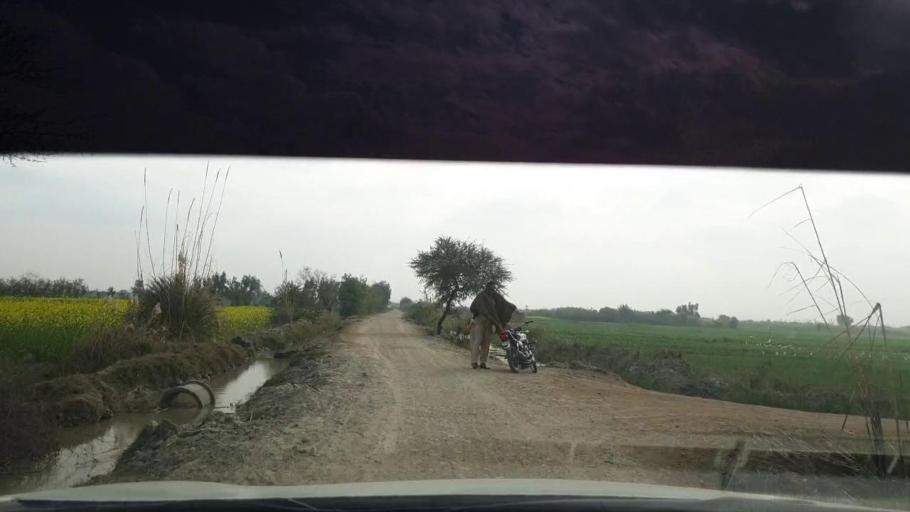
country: PK
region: Sindh
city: Berani
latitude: 25.7528
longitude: 68.8769
